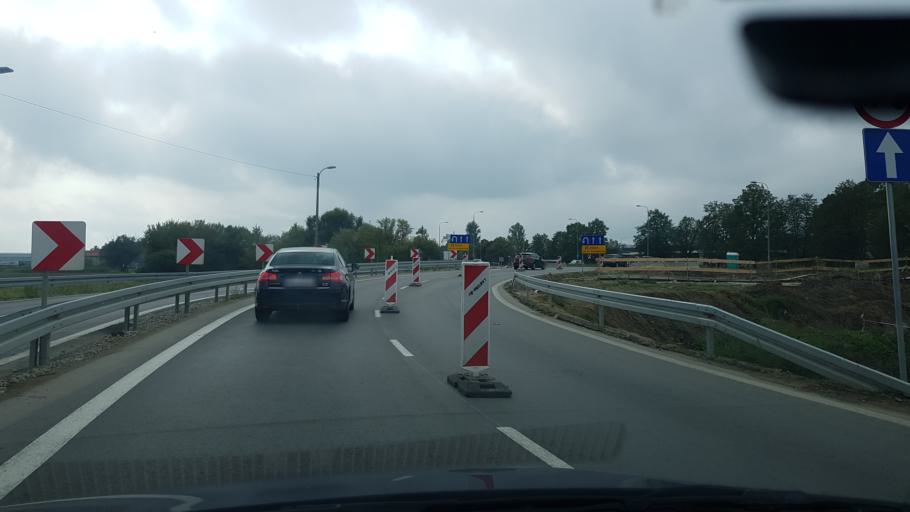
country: PL
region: Masovian Voivodeship
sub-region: Warszawa
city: Wilanow
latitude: 52.1501
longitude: 21.0926
